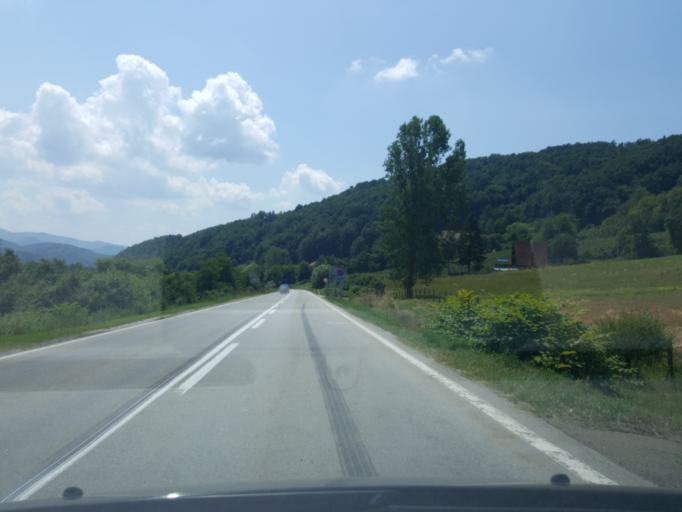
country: RS
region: Central Serbia
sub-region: Moravicki Okrug
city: Gornji Milanovac
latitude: 44.0875
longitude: 20.4793
